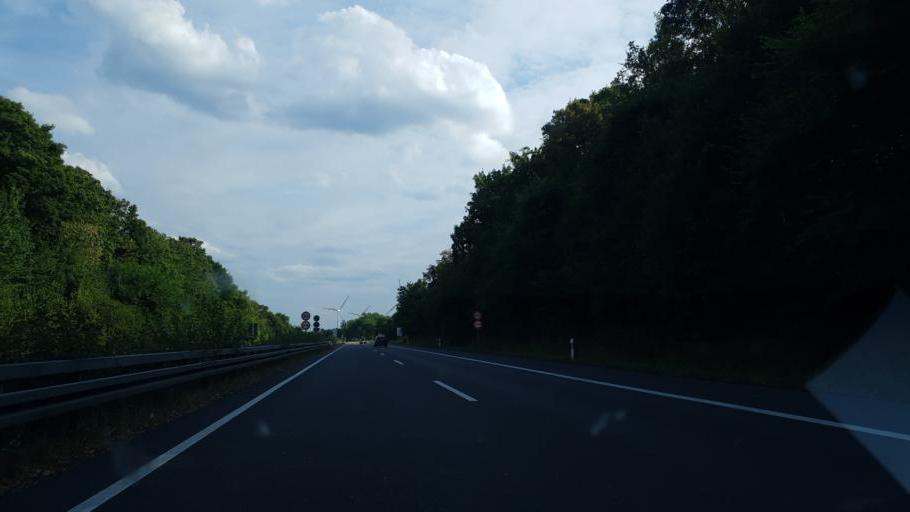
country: DE
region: Lower Saxony
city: Holle
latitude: 52.0942
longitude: 10.1822
